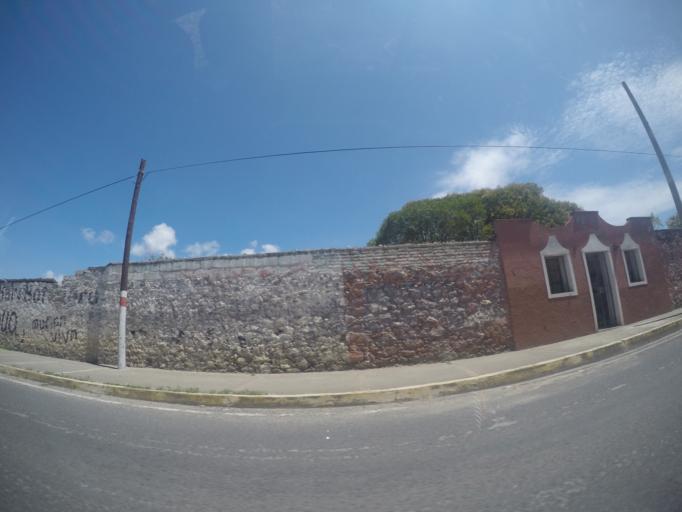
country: MX
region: Hidalgo
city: Mineral del Monte
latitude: 20.1395
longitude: -98.6872
